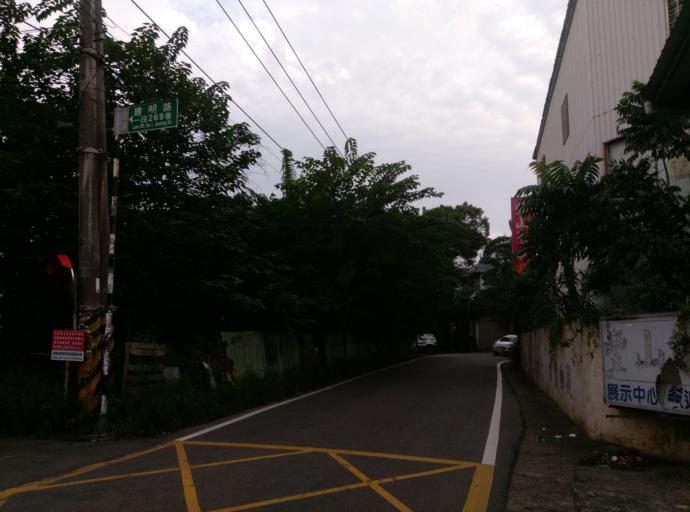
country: TW
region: Taiwan
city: Daxi
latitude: 24.9175
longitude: 121.2387
